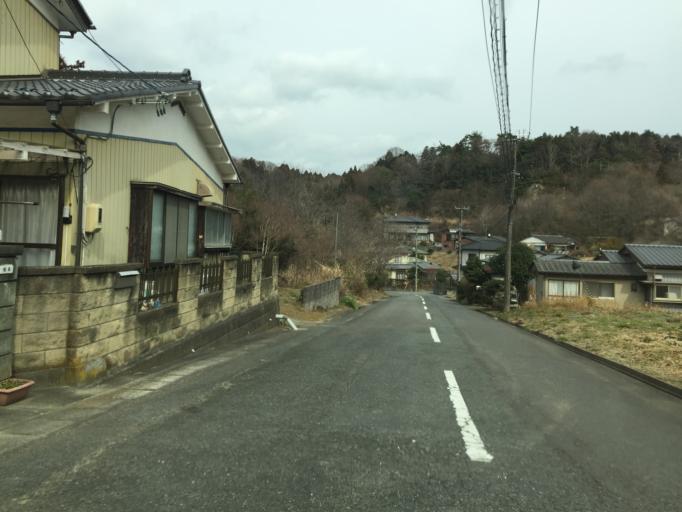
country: JP
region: Ibaraki
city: Kitaibaraki
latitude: 36.8745
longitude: 140.7837
